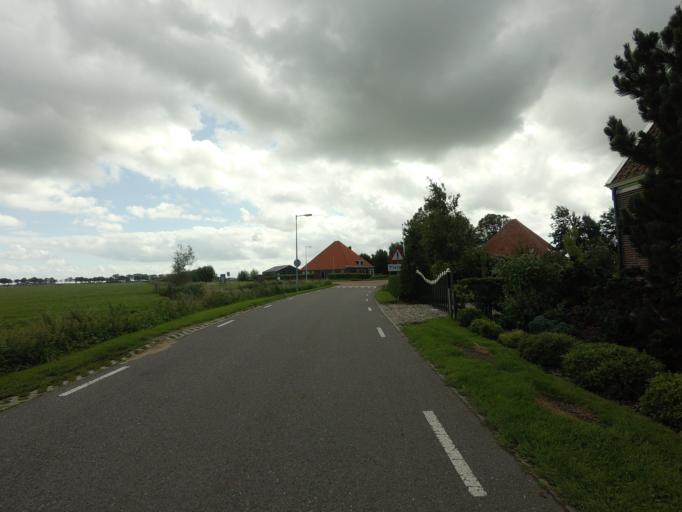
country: NL
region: North Holland
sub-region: Gemeente Edam-Volendam
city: Edam
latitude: 52.5450
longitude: 5.0097
